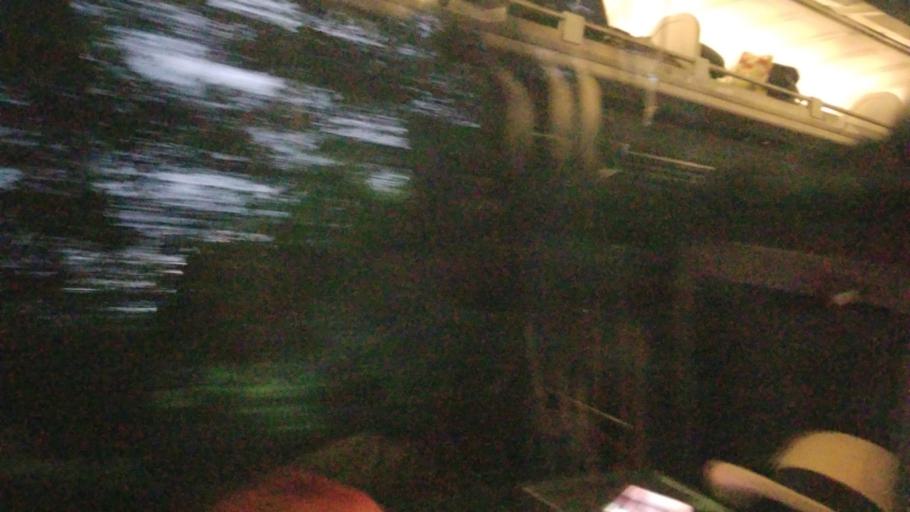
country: US
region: Virginia
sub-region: Orange County
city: Gordonsville
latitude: 38.1871
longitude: -78.2495
